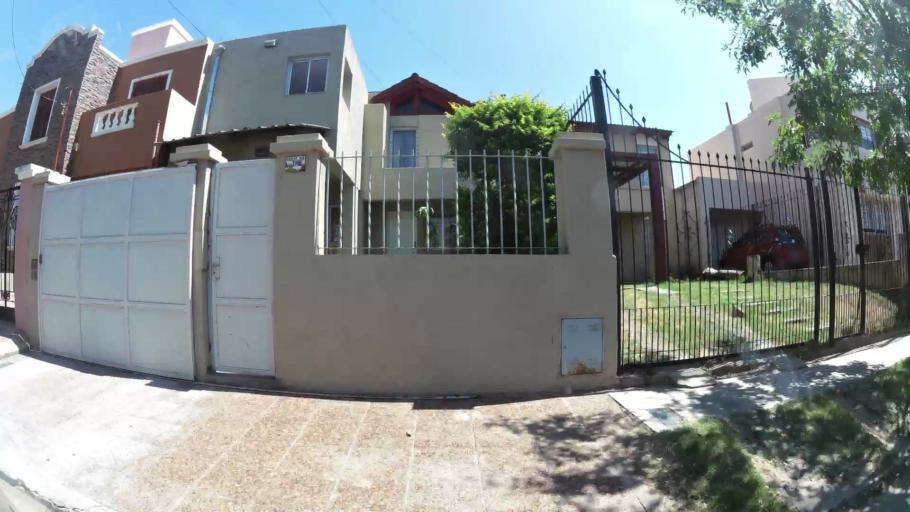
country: AR
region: Cordoba
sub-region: Departamento de Capital
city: Cordoba
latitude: -31.4574
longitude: -64.1628
